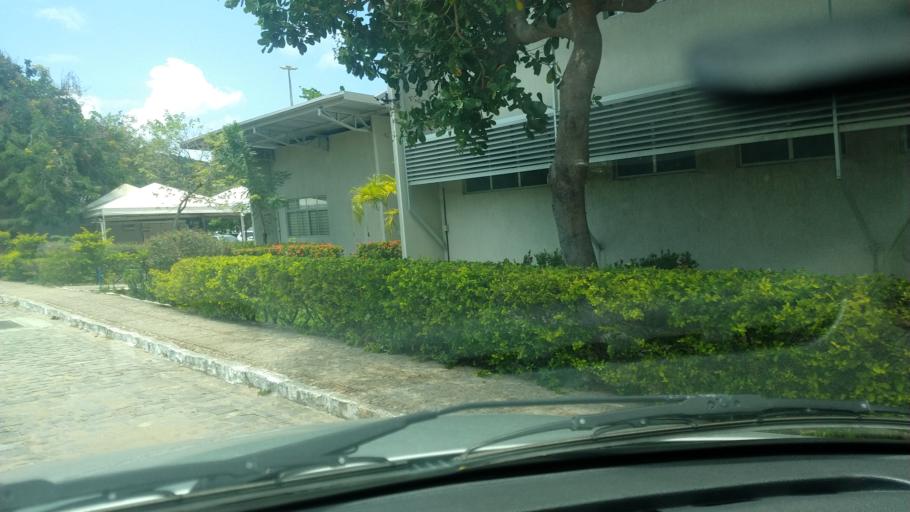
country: BR
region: Rio Grande do Norte
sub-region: Natal
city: Natal
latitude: -5.8431
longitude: -35.1992
